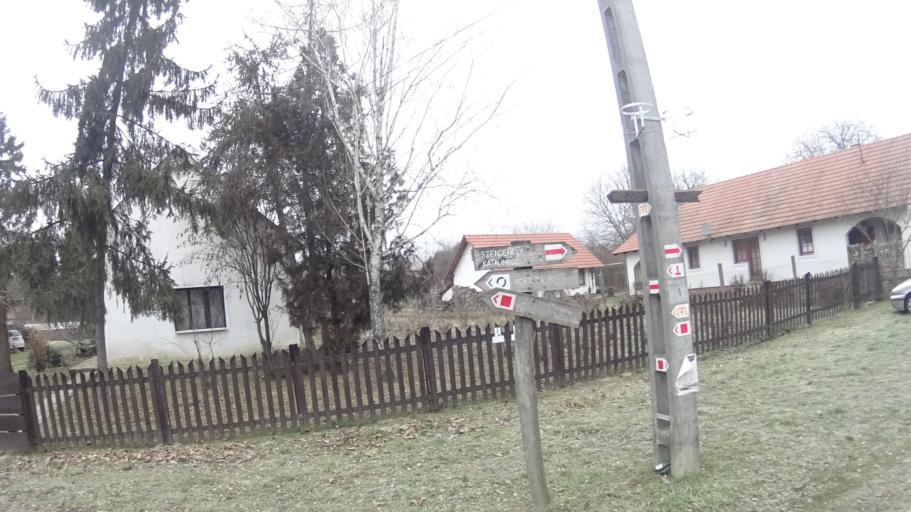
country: HU
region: Pest
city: Kosd
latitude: 47.8119
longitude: 19.1816
